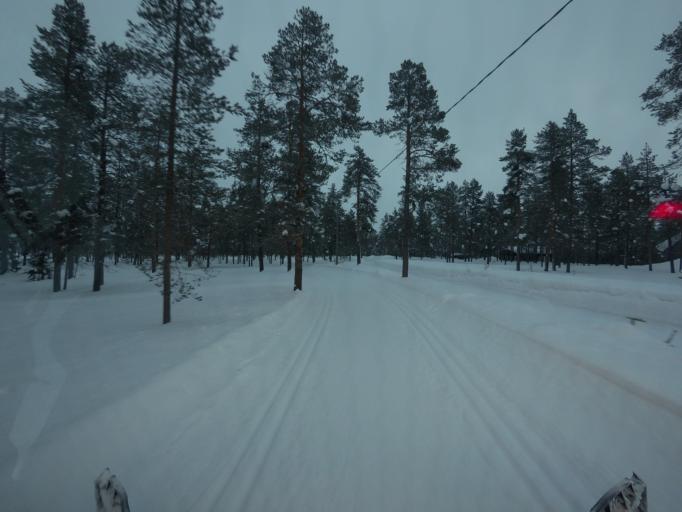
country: FI
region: Lapland
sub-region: Tunturi-Lappi
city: Kolari
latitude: 67.6230
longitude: 24.1743
